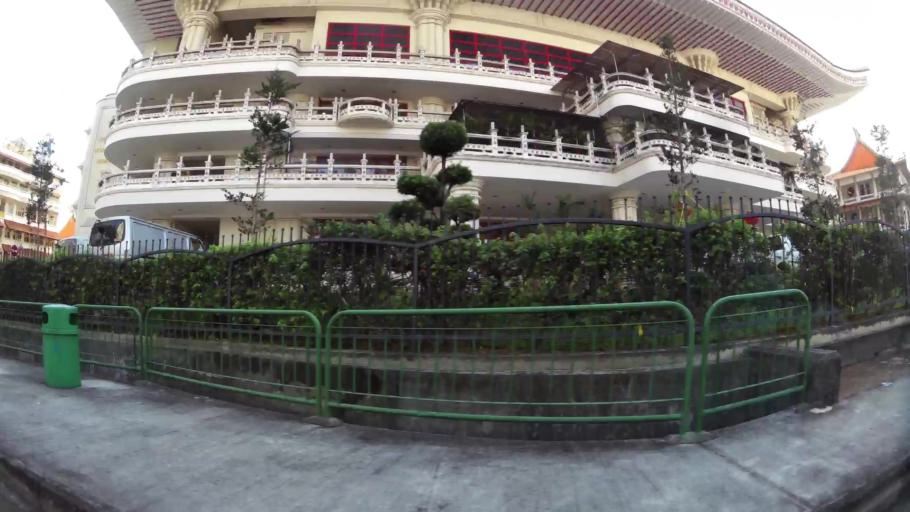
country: SG
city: Singapore
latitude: 1.3618
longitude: 103.8354
